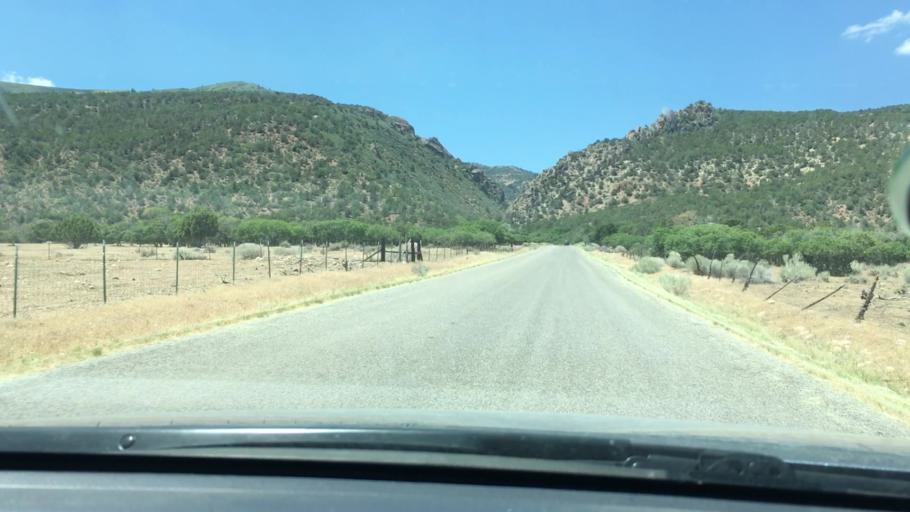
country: US
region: Utah
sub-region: Sanpete County
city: Moroni
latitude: 39.5559
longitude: -111.6538
